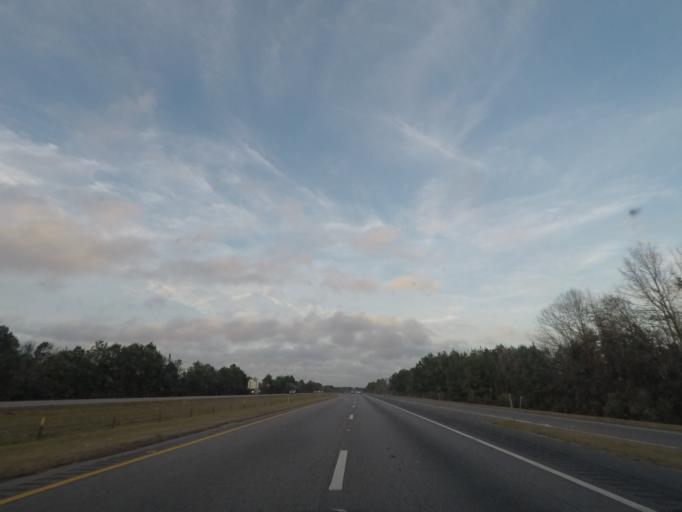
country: US
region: South Carolina
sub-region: Orangeburg County
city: Holly Hill
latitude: 33.3864
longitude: -80.5174
